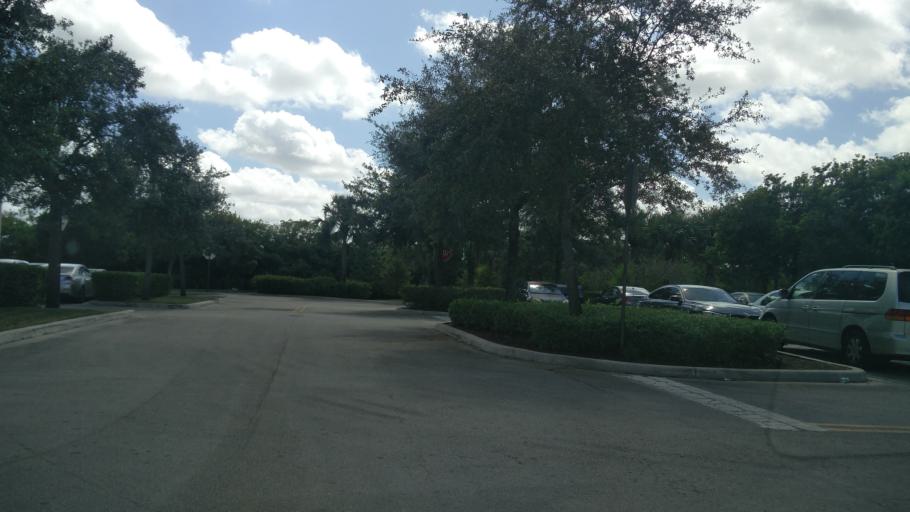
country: US
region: Florida
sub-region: Broward County
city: Cooper City
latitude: 26.0058
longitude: -80.2902
